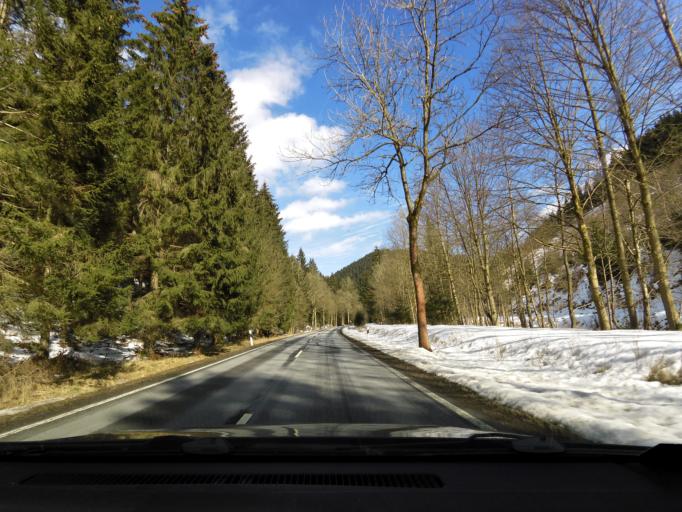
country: DE
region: Lower Saxony
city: Sankt Andreasberg
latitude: 51.6876
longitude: 10.4983
